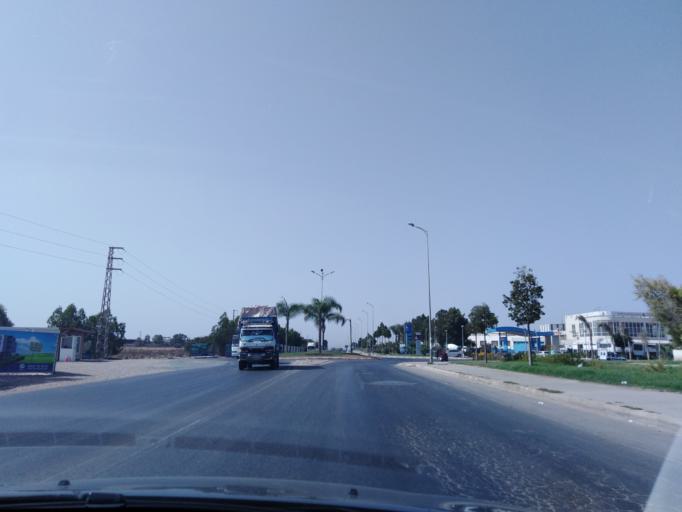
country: MA
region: Chaouia-Ouardigha
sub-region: Settat Province
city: Berrechid
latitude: 33.2531
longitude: -7.5839
